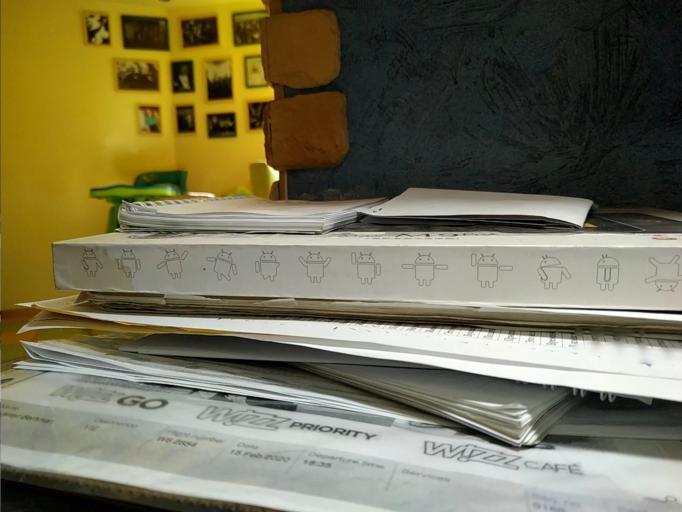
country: RU
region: Novgorod
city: Volot
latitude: 57.7514
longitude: 30.5960
